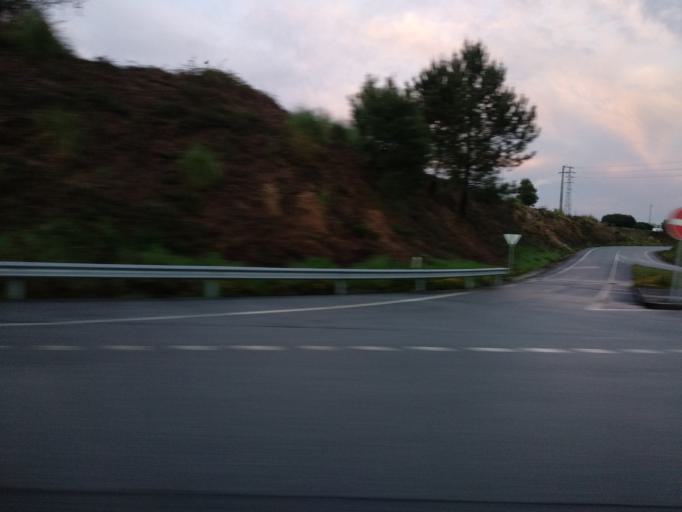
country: PT
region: Braga
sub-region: Vila Nova de Famalicao
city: Calendario
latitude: 41.3891
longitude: -8.5182
